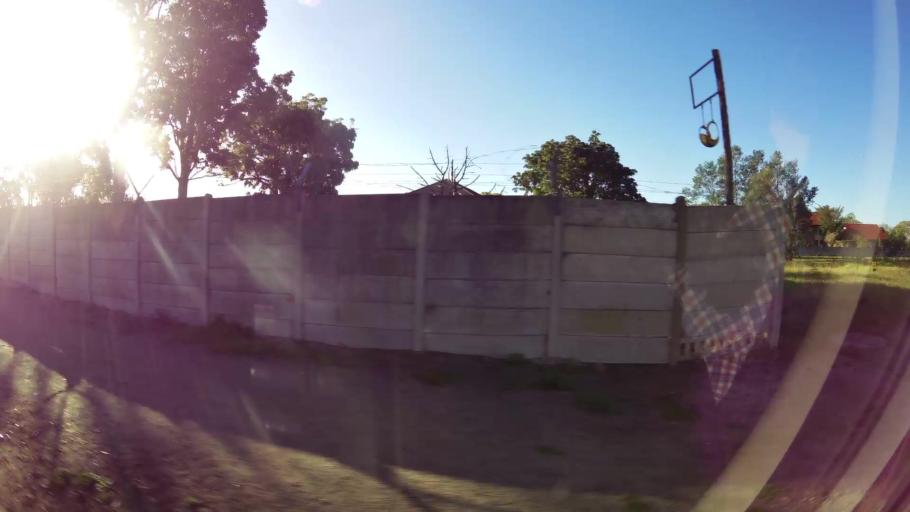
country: ZA
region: Western Cape
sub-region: Eden District Municipality
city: George
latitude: -33.9549
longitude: 22.4462
